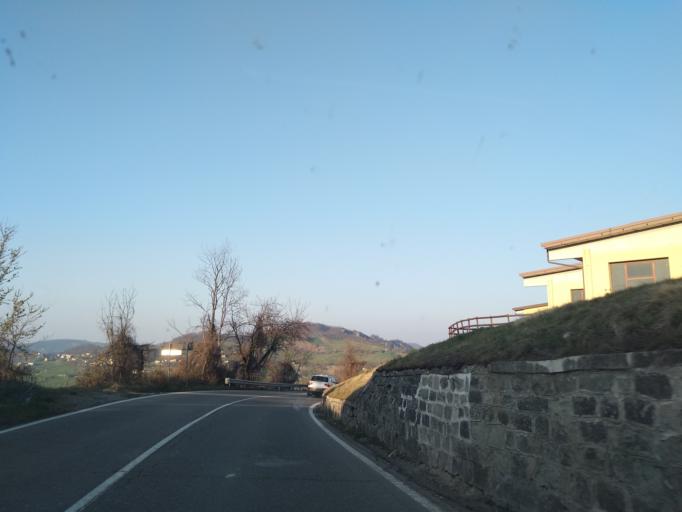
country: IT
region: Emilia-Romagna
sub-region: Provincia di Reggio Emilia
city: Castelnovo ne'Monti
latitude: 44.4323
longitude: 10.4175
